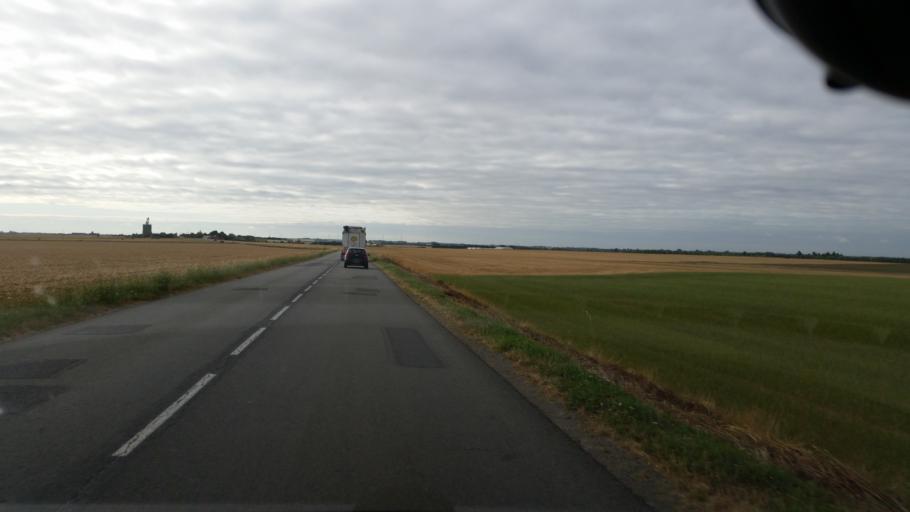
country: FR
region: Poitou-Charentes
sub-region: Departement de la Charente-Maritime
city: Marans
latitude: 46.2953
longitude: -0.9691
